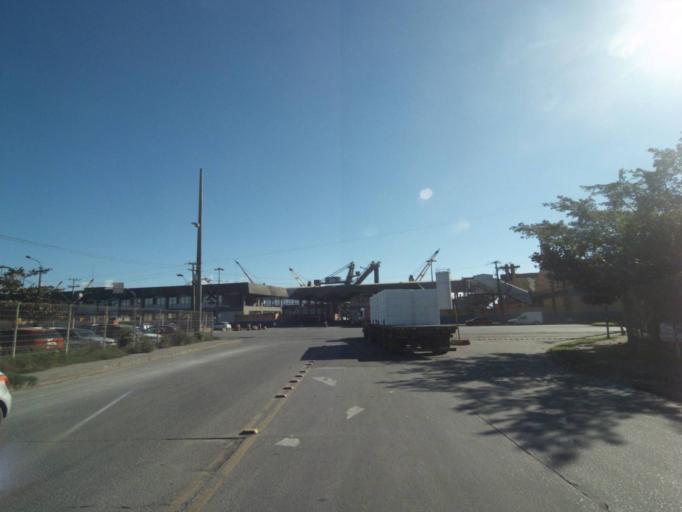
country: BR
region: Parana
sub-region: Paranagua
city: Paranagua
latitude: -25.5042
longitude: -48.5187
